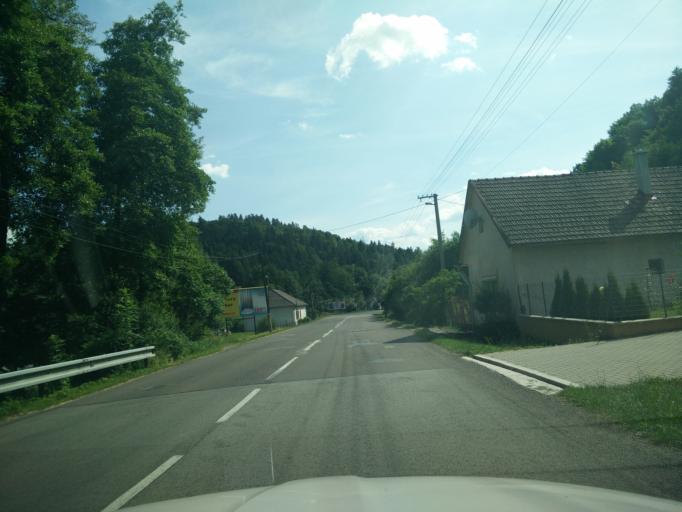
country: SK
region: Nitriansky
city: Prievidza
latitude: 48.9016
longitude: 18.6497
